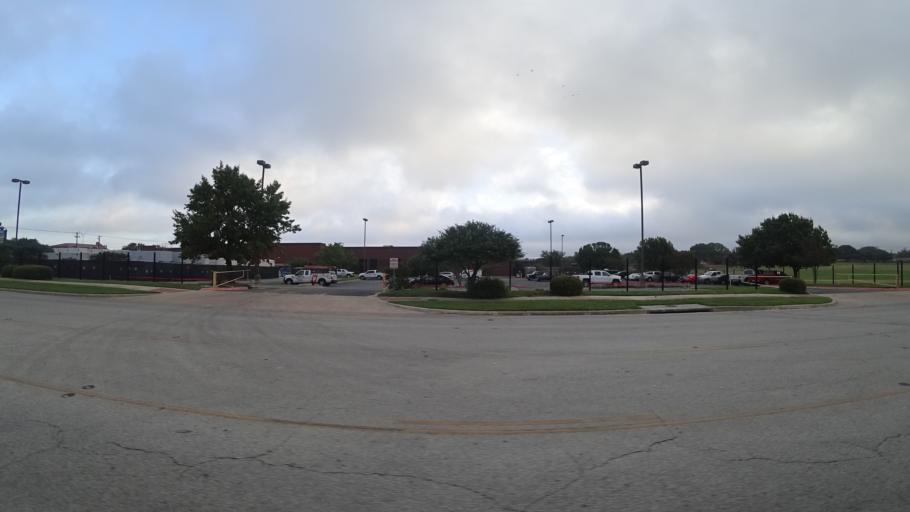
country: US
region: Texas
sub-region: Travis County
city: Austin
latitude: 30.3417
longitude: -97.6965
